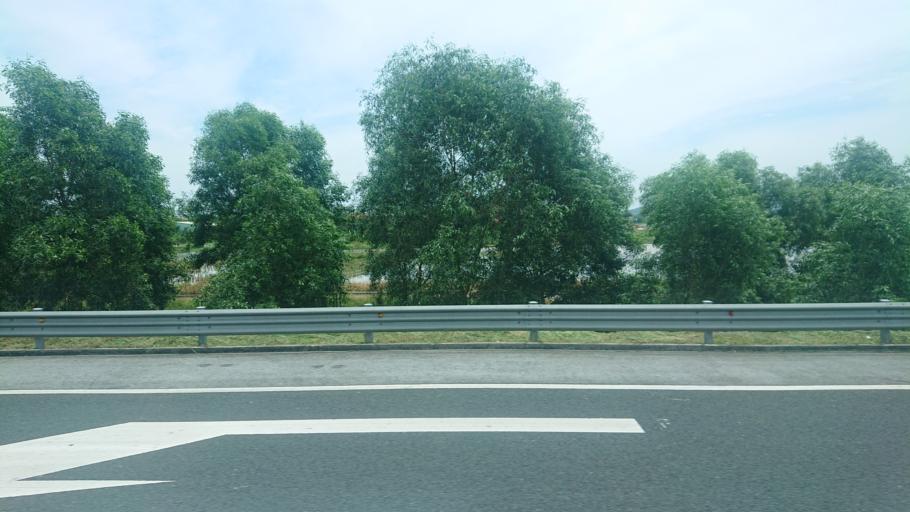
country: VN
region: Hai Phong
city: An Lao
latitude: 20.7956
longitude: 106.5446
